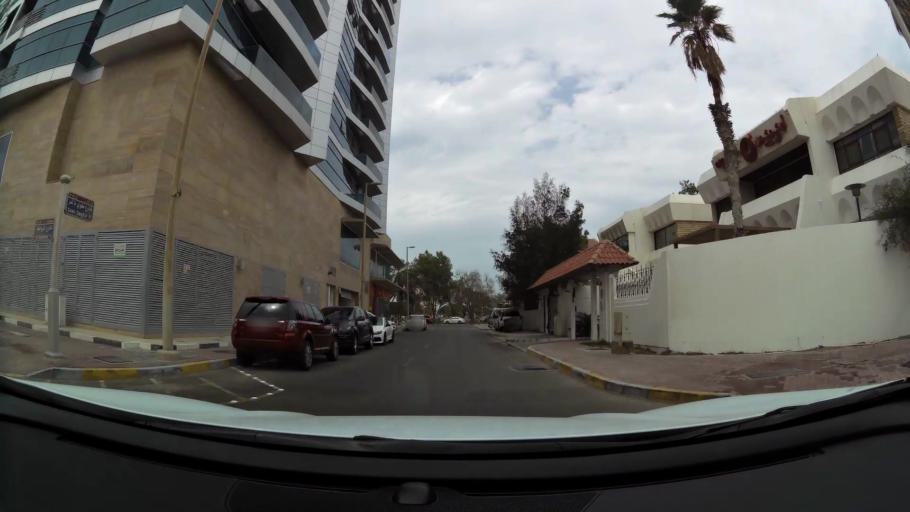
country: AE
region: Abu Dhabi
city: Abu Dhabi
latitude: 24.4675
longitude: 54.3352
